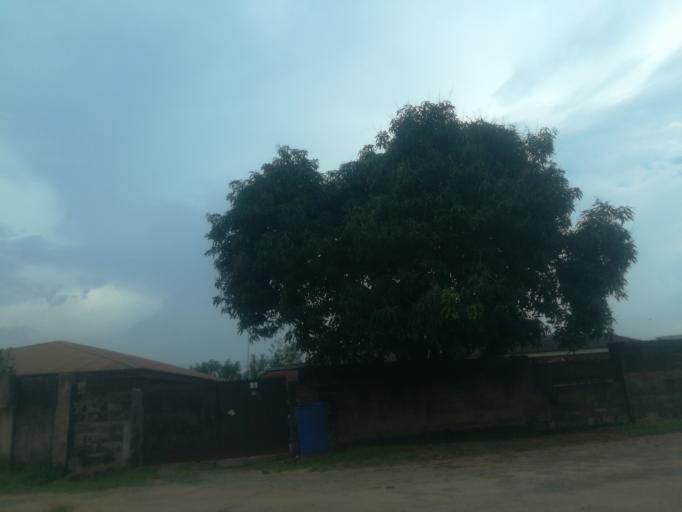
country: NG
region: Oyo
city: Ibadan
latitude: 7.4157
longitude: 3.9020
